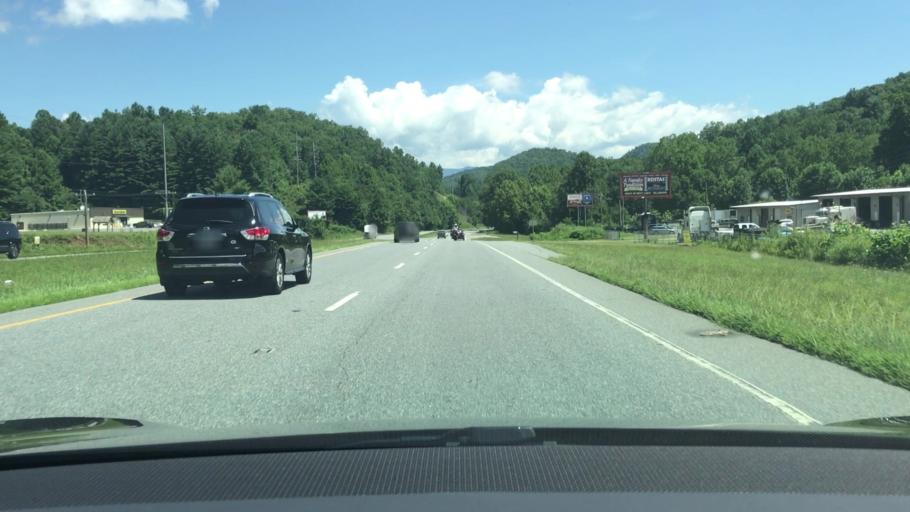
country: US
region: North Carolina
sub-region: Jackson County
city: Sylva
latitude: 35.2977
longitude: -83.2640
